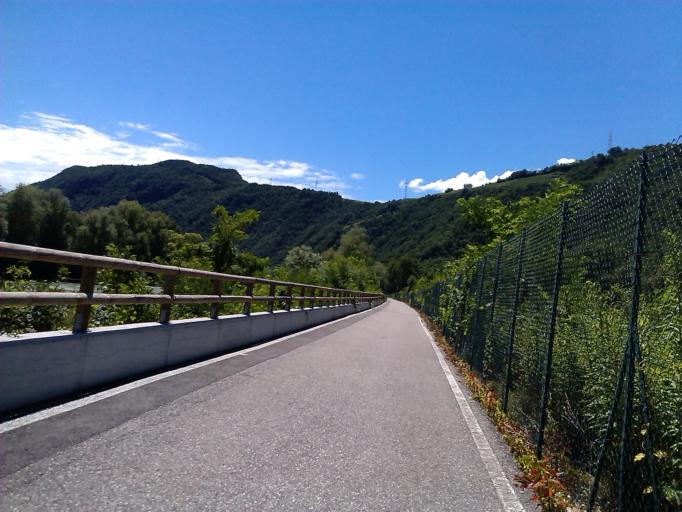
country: IT
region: Trentino-Alto Adige
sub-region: Bolzano
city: Cornaiano
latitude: 46.4666
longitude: 11.3051
